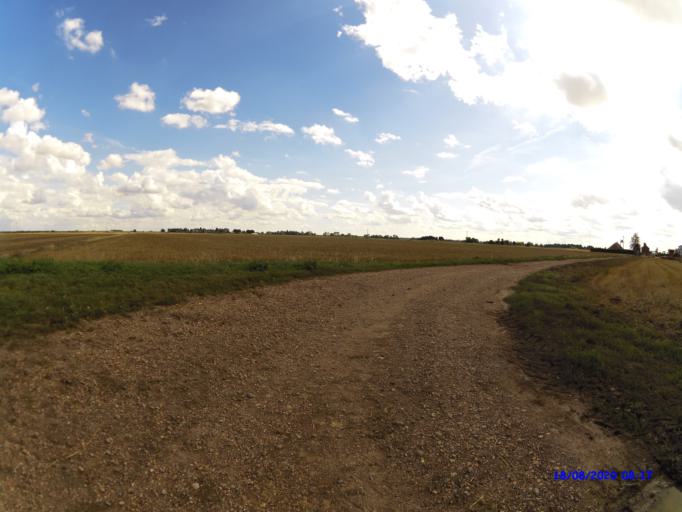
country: GB
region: England
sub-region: Cambridgeshire
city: Ramsey
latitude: 52.5055
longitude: -0.0773
